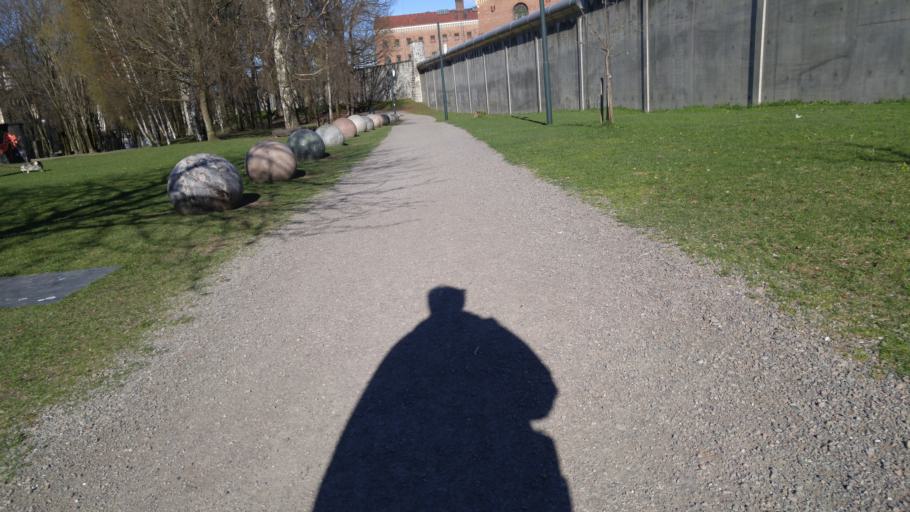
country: NO
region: Oslo
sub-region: Oslo
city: Oslo
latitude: 59.9085
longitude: 10.7738
